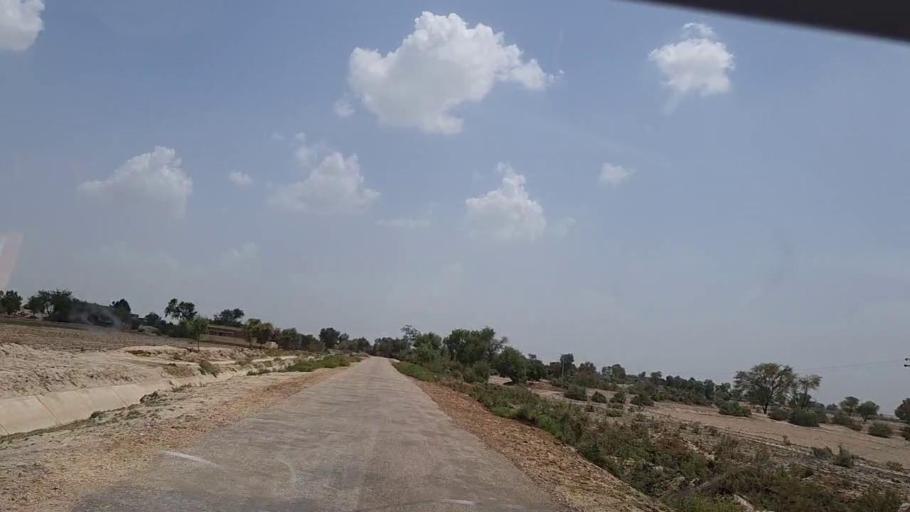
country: PK
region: Sindh
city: Bhan
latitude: 26.5159
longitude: 67.6394
